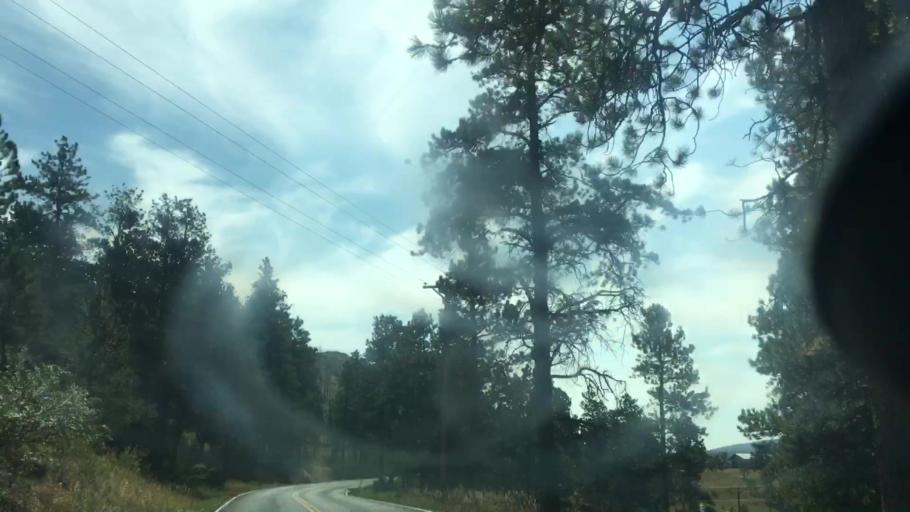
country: US
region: Colorado
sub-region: Larimer County
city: Laporte
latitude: 40.5932
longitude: -105.3379
